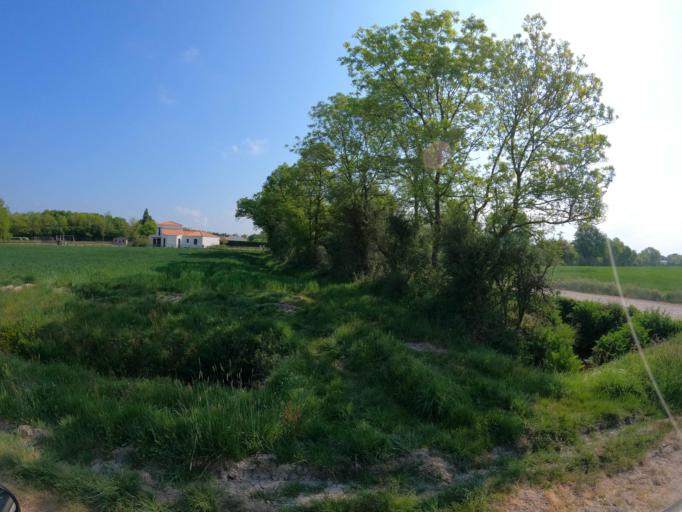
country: FR
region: Pays de la Loire
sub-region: Departement de la Vendee
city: Treize-Septiers
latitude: 46.9990
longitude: -1.2414
